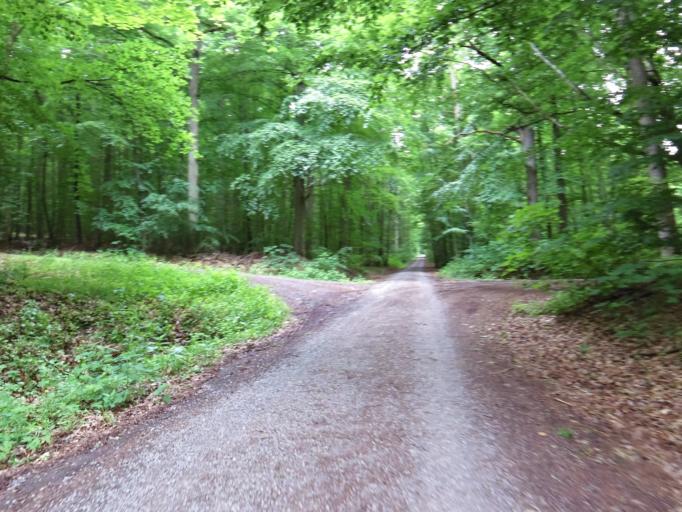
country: DE
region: Bavaria
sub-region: Regierungsbezirk Unterfranken
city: Kist
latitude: 49.7345
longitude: 9.8669
